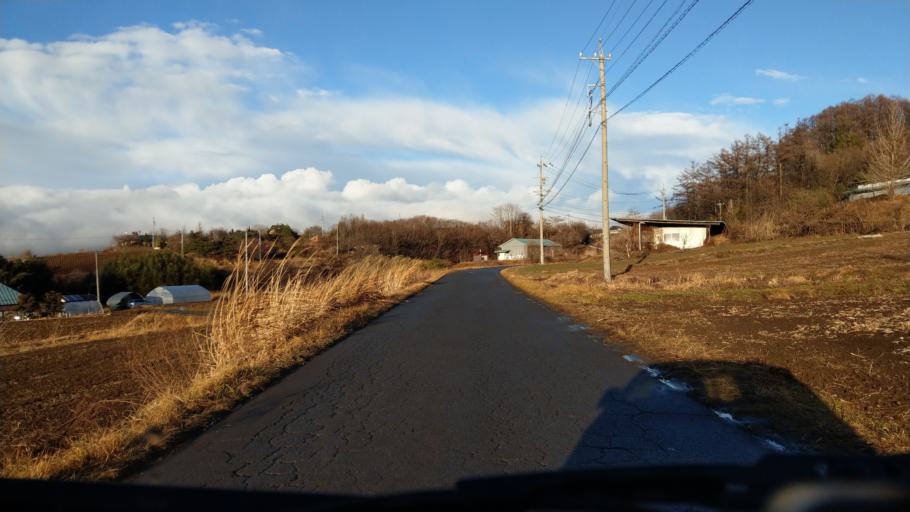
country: JP
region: Nagano
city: Komoro
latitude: 36.3064
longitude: 138.3592
